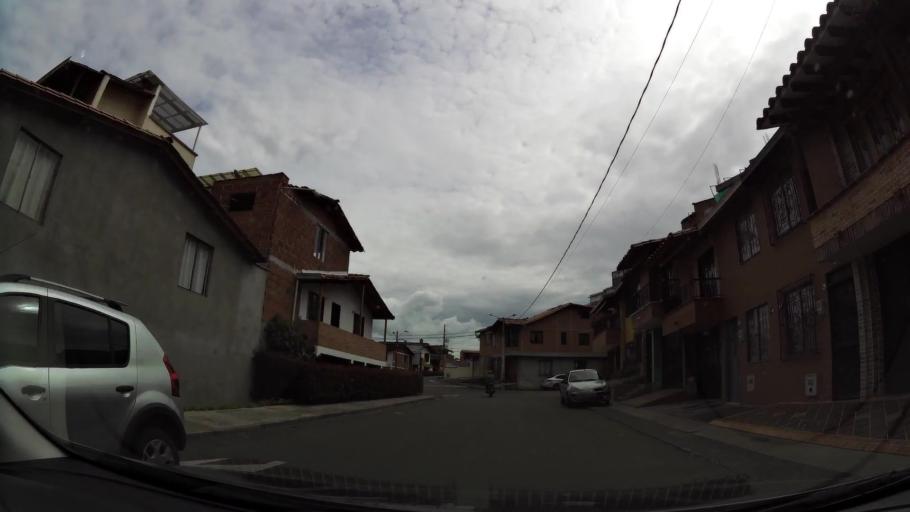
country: CO
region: Antioquia
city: Rionegro
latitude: 6.1598
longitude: -75.3734
